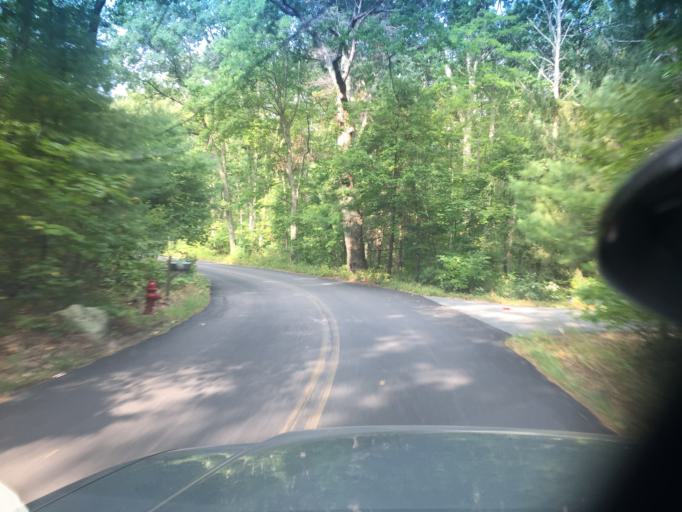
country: US
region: Massachusetts
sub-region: Norfolk County
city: Bellingham
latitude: 42.1321
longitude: -71.4633
